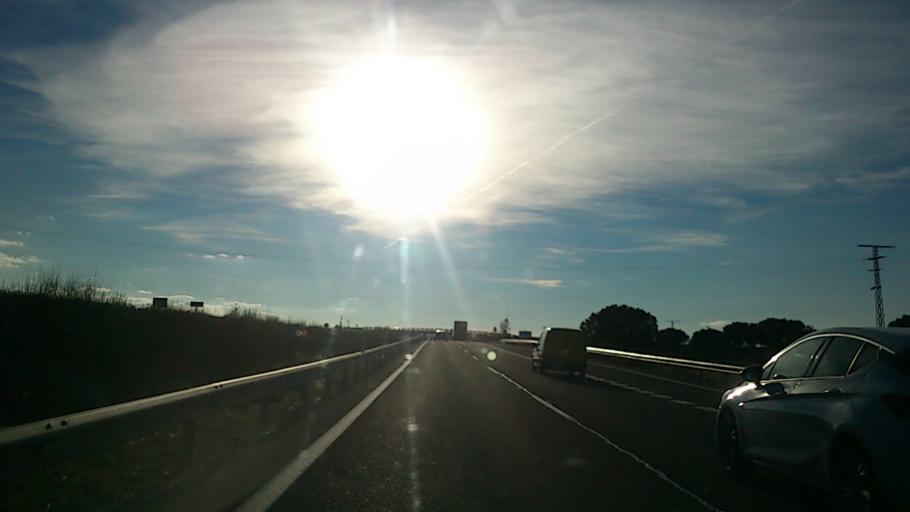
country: ES
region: Castille-La Mancha
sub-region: Provincia de Guadalajara
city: Mirabueno
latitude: 40.9329
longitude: -2.7103
